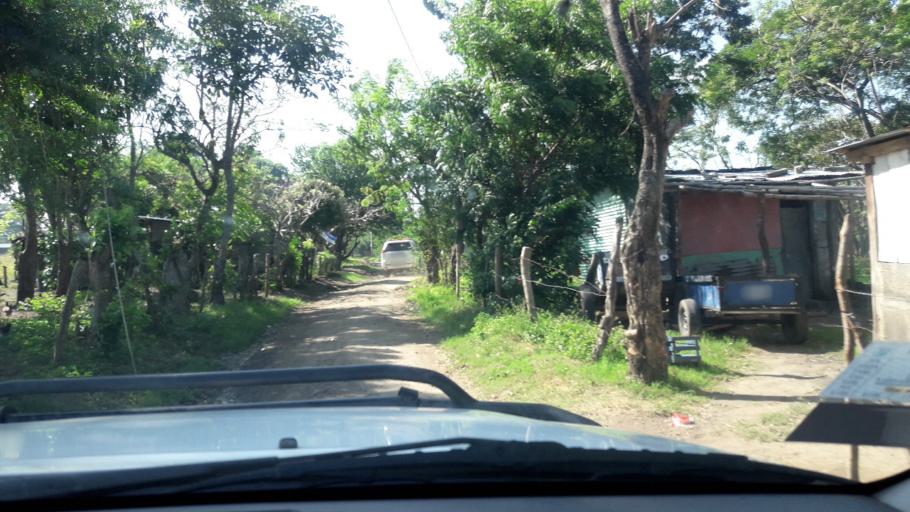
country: NI
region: Rivas
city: Belen
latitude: 11.5419
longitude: -85.8989
